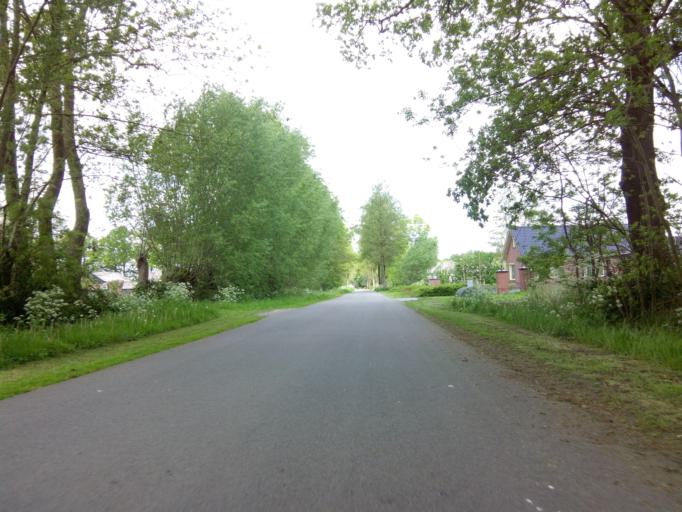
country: NL
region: Gelderland
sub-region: Gemeente Ede
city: Lunteren
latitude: 52.0665
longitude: 5.6264
